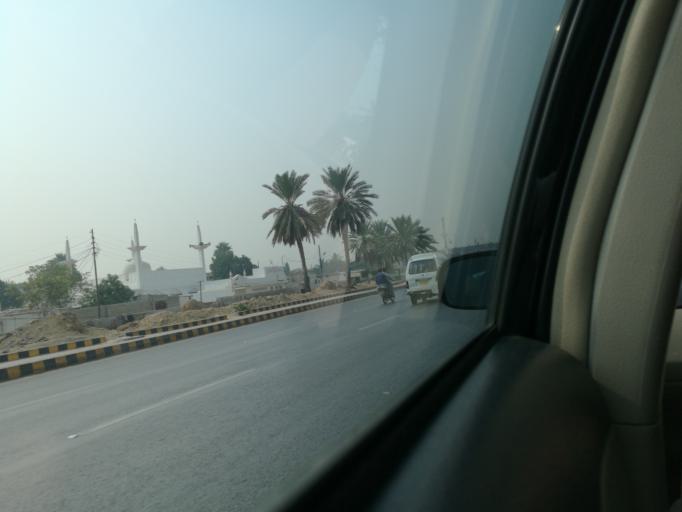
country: PK
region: Sindh
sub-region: Karachi District
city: Karachi
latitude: 24.8758
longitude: 67.0993
